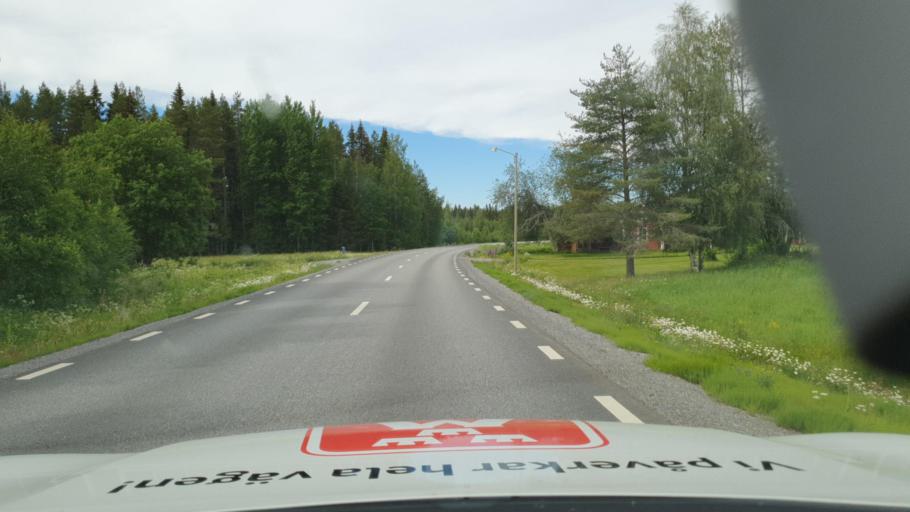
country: SE
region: Vaesterbotten
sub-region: Skelleftea Kommun
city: Burtraesk
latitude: 64.4993
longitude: 20.6266
